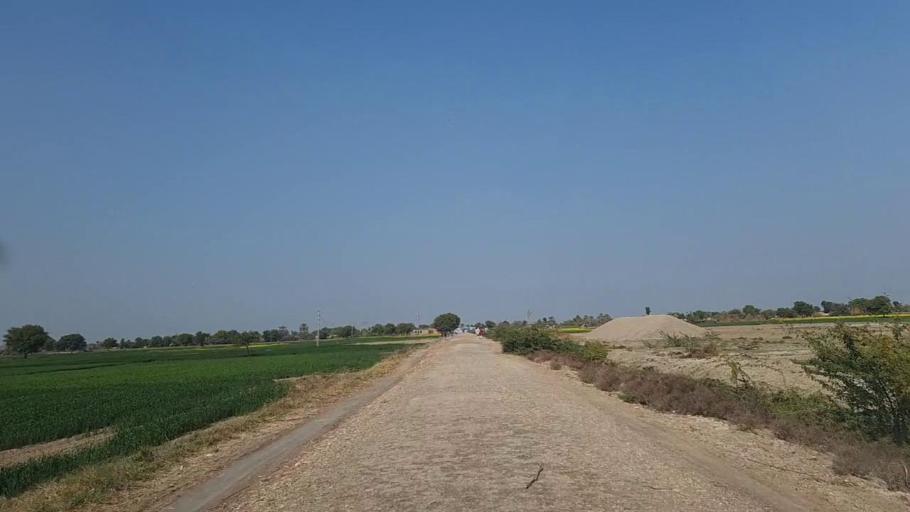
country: PK
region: Sindh
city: Jam Sahib
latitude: 26.2705
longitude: 68.5288
